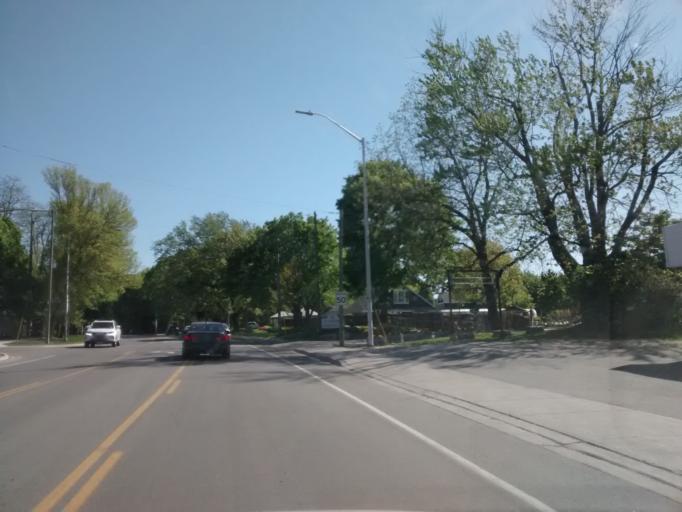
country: CA
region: Ontario
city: Oakville
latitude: 43.3879
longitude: -79.7167
